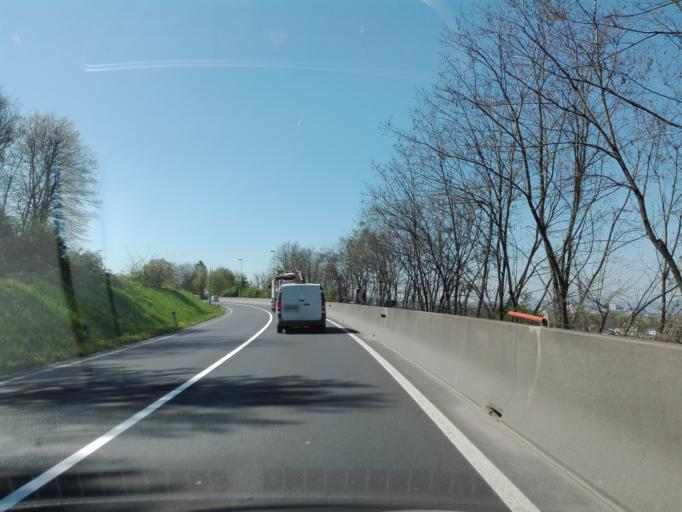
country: AT
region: Upper Austria
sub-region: Politischer Bezirk Urfahr-Umgebung
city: Steyregg
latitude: 48.2508
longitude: 14.3534
